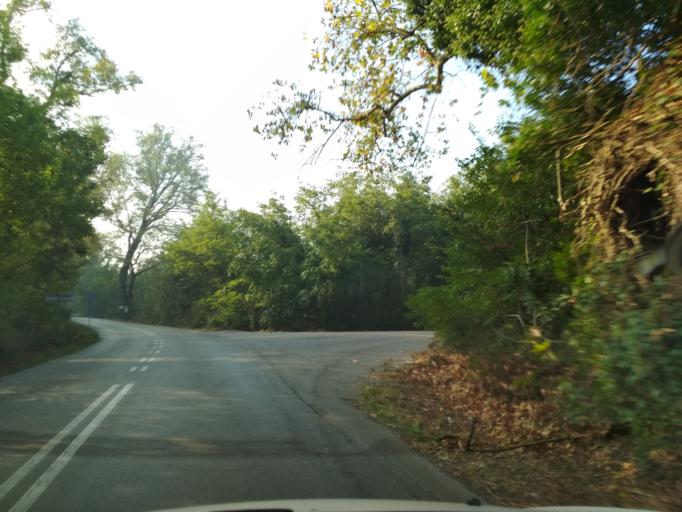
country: GR
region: Central Greece
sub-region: Nomos Evvoias
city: Prokopion
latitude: 38.7414
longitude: 23.4902
